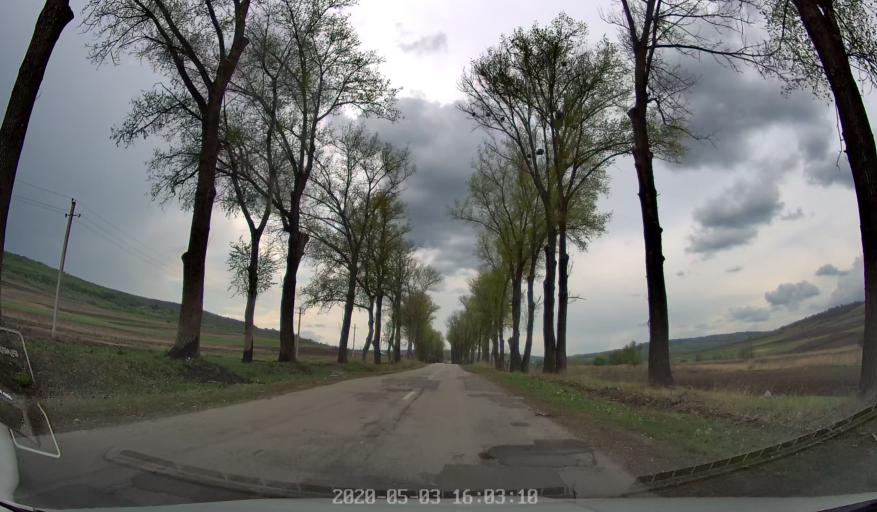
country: MD
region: Stinga Nistrului
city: Bucovat
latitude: 47.1780
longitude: 28.3853
